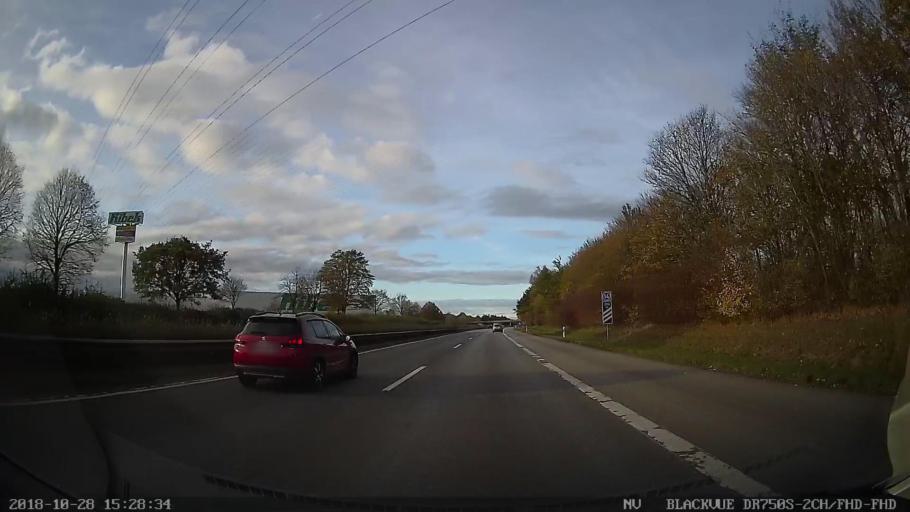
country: DE
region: Schleswig-Holstein
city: Seeth-Ekholt
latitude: 53.7390
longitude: 9.7160
